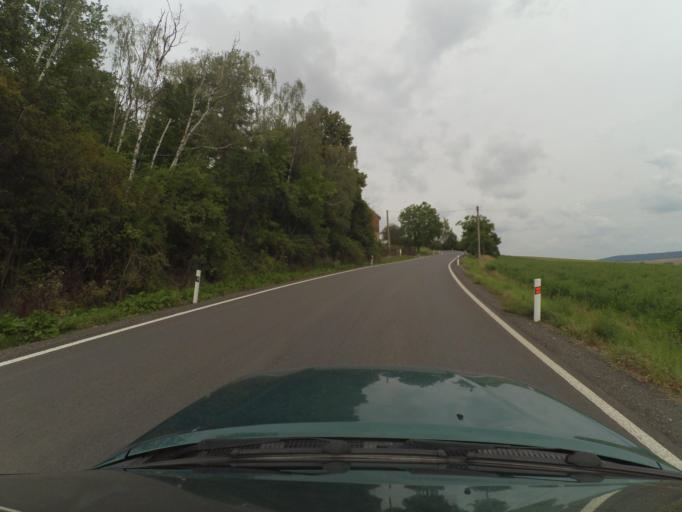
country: CZ
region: Central Bohemia
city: Revnicov
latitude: 50.1979
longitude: 13.7443
